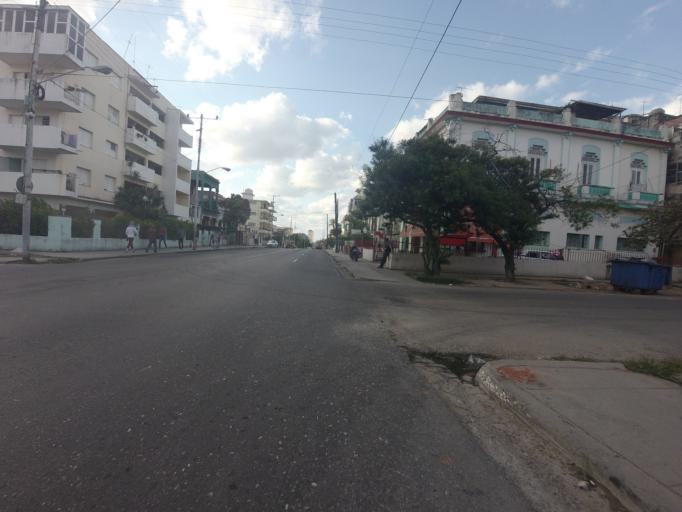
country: CU
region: La Habana
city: Havana
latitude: 23.1282
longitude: -82.4005
